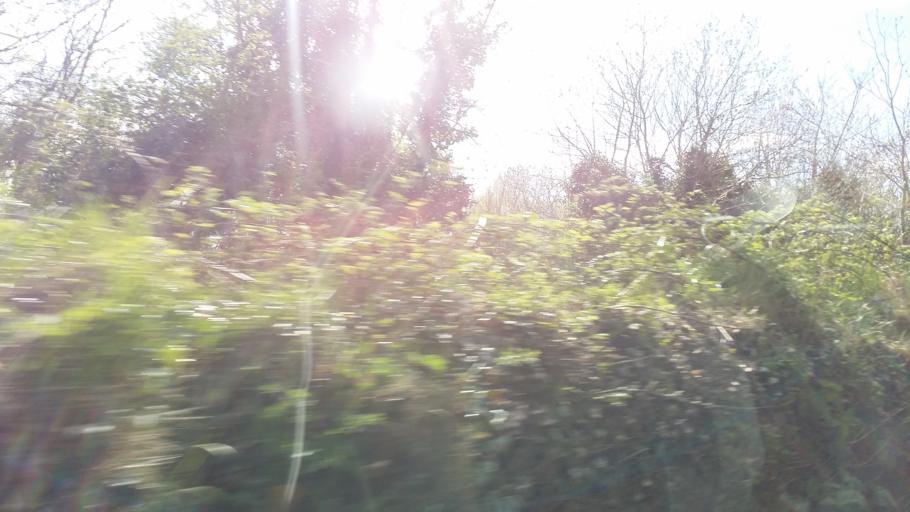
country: IE
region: Ulster
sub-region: County Donegal
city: Ballyshannon
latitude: 54.4895
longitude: -8.1455
